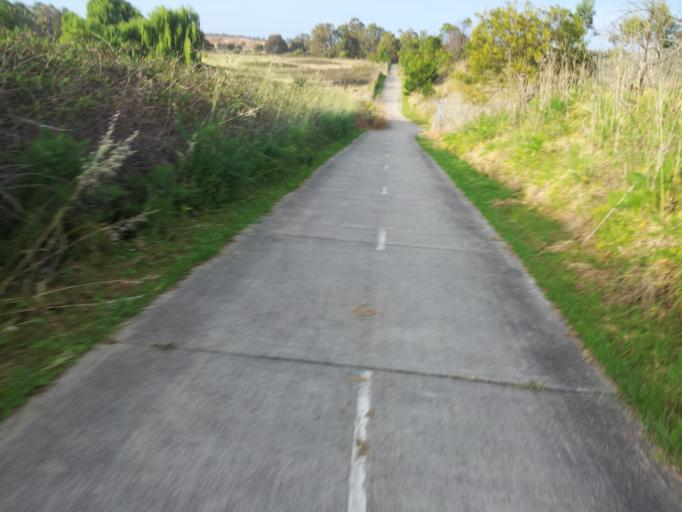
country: AU
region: New South Wales
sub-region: Fairfield
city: Horsley Park
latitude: -33.8359
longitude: 150.8776
